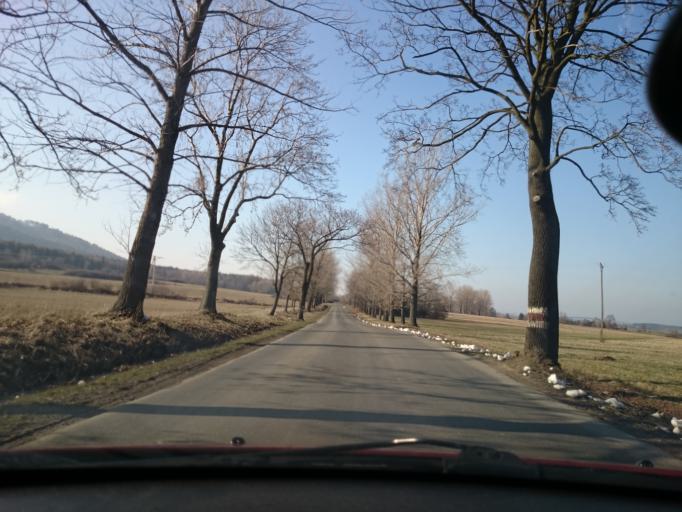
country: PL
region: Lower Silesian Voivodeship
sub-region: Powiat klodzki
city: Bystrzyca Klodzka
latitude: 50.3154
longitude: 16.6165
